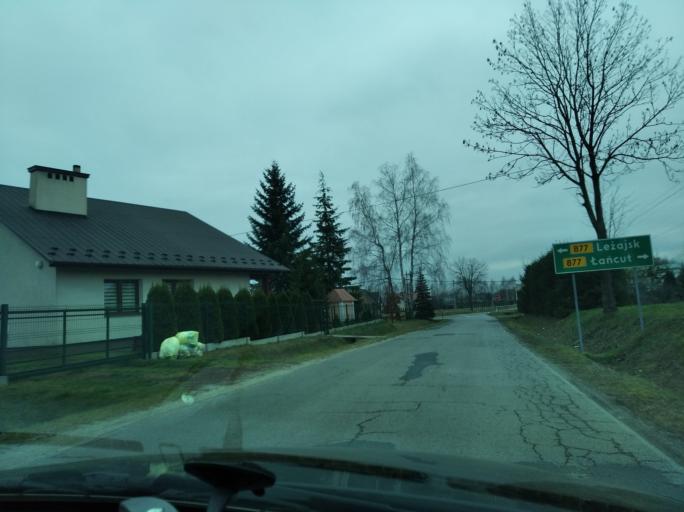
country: PL
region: Subcarpathian Voivodeship
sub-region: Powiat lancucki
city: Zolynia
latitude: 50.1796
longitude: 22.3119
